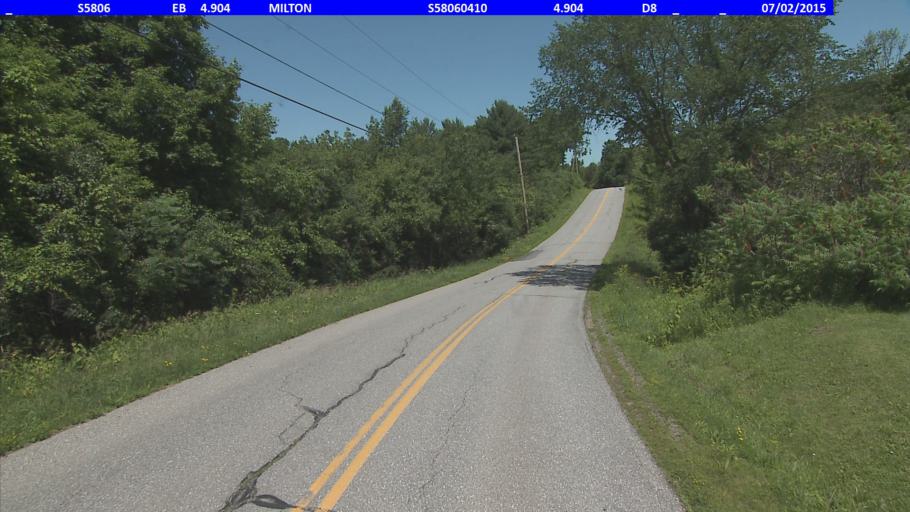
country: US
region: Vermont
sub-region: Chittenden County
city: Milton
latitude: 44.6912
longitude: -73.1788
